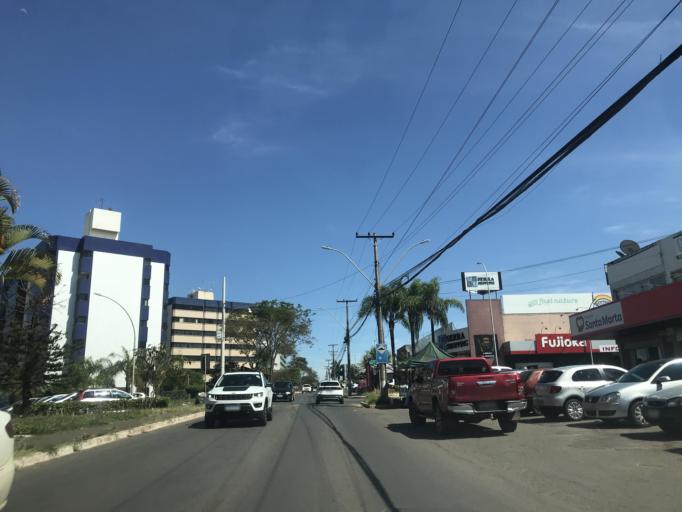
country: BR
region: Federal District
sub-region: Brasilia
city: Brasilia
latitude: -15.6519
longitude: -47.7897
